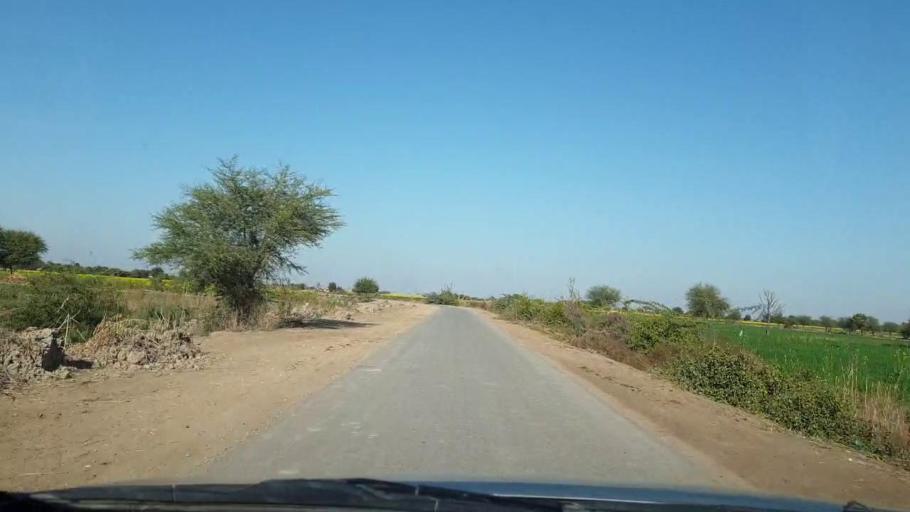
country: PK
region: Sindh
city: Jhol
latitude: 25.8276
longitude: 68.9491
